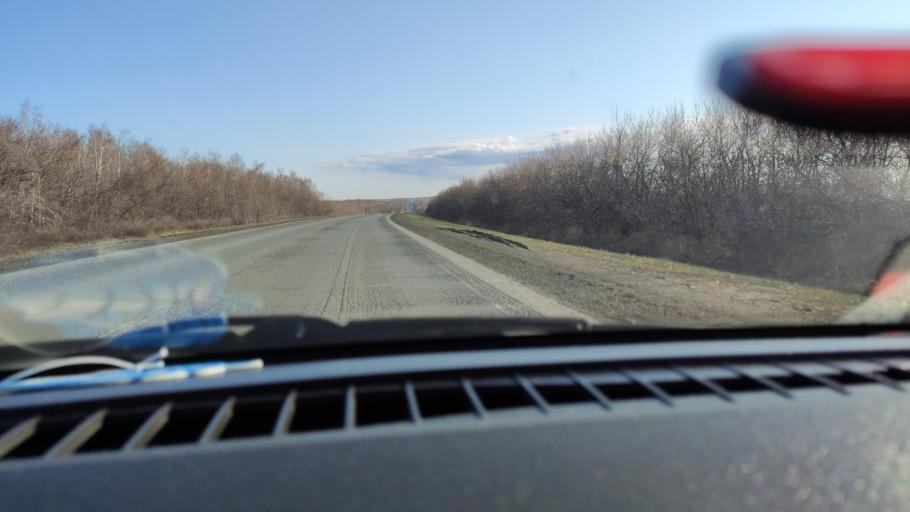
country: RU
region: Saratov
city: Dukhovnitskoye
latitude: 52.6504
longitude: 48.1992
